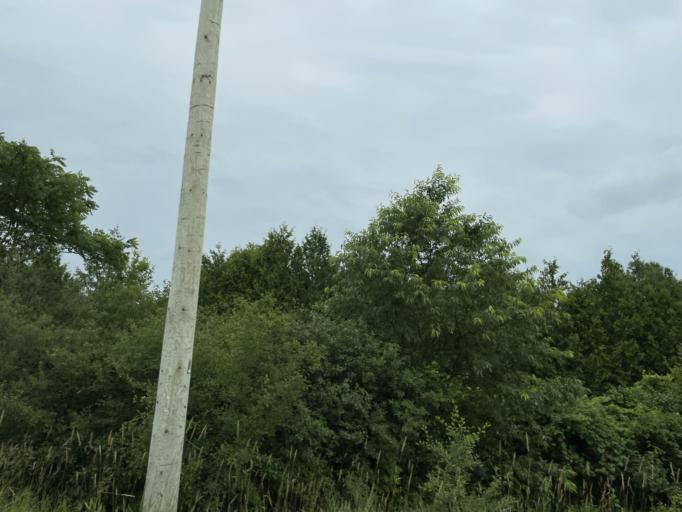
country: CA
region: Ontario
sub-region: Wellington County
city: Guelph
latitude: 43.5938
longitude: -80.2734
